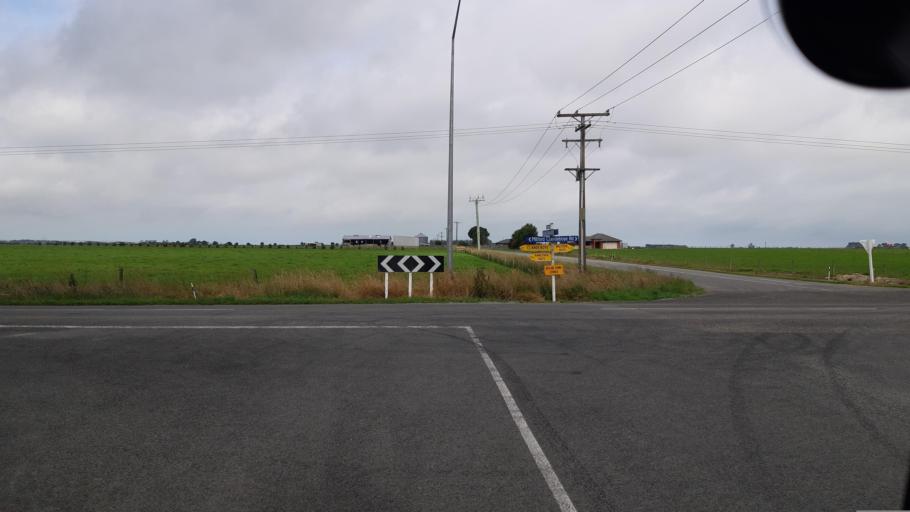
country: NZ
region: Canterbury
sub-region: Timaru District
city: Timaru
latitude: -44.2479
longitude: 171.3411
